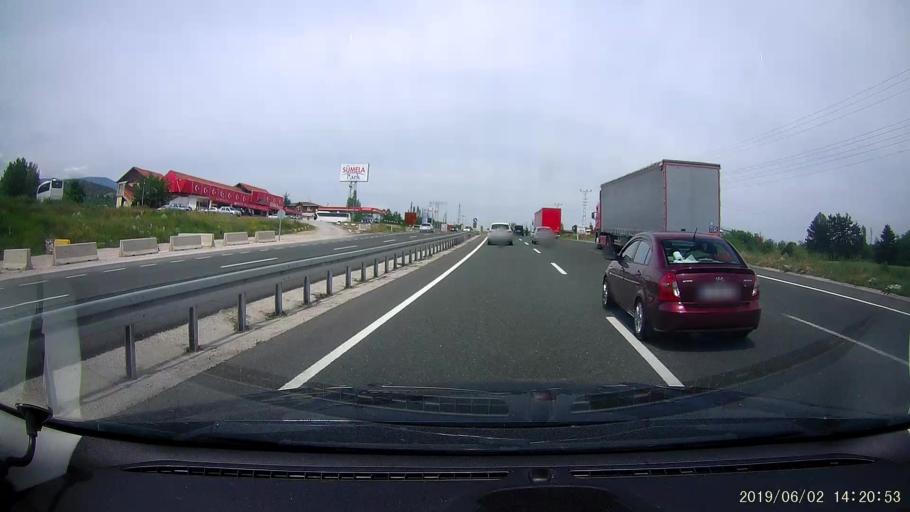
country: TR
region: Kastamonu
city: Tosya
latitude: 40.9735
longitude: 33.9975
